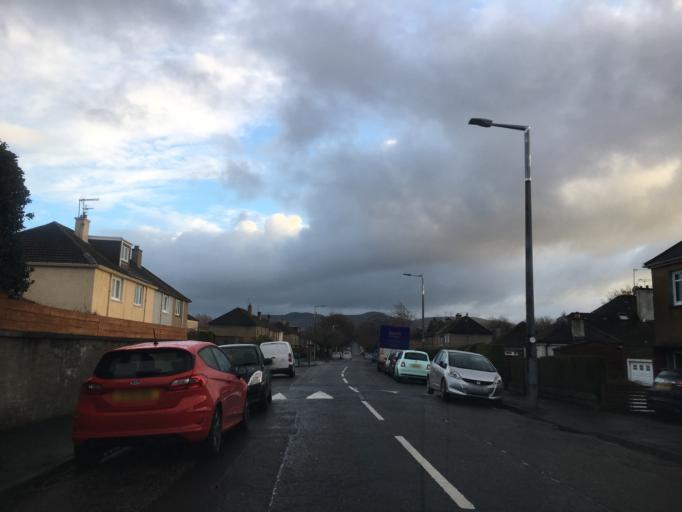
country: GB
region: Scotland
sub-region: Edinburgh
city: Colinton
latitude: 55.9402
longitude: -3.2711
